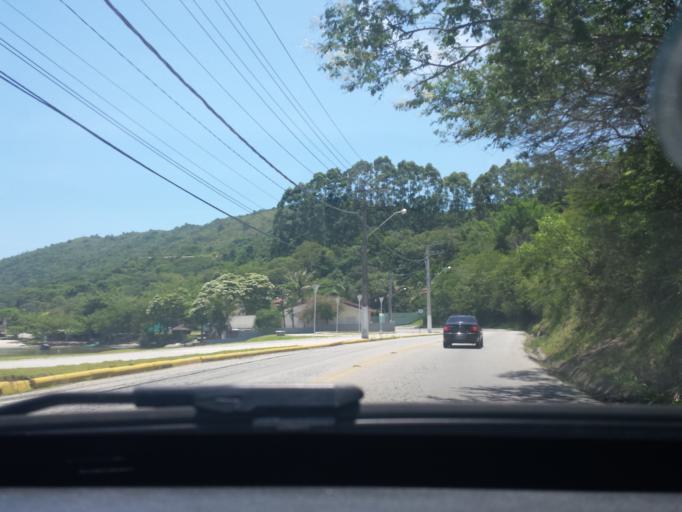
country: BR
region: Santa Catarina
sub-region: Porto Belo
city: Porto Belo
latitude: -27.1473
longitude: -48.5340
